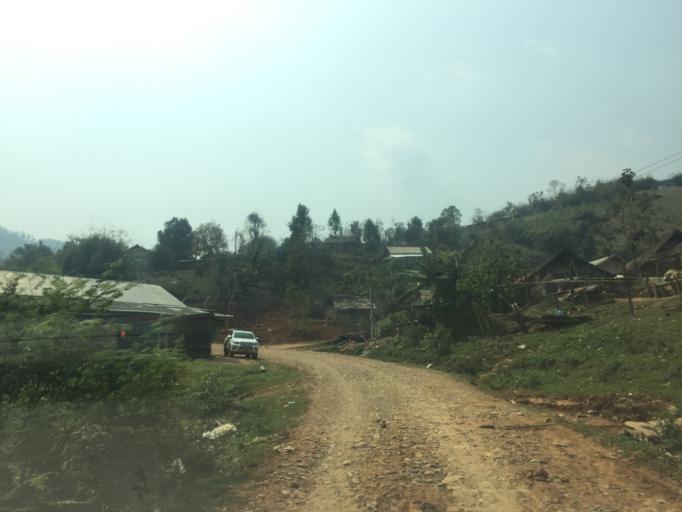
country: TH
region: Phayao
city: Phu Sang
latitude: 19.5681
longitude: 100.5248
